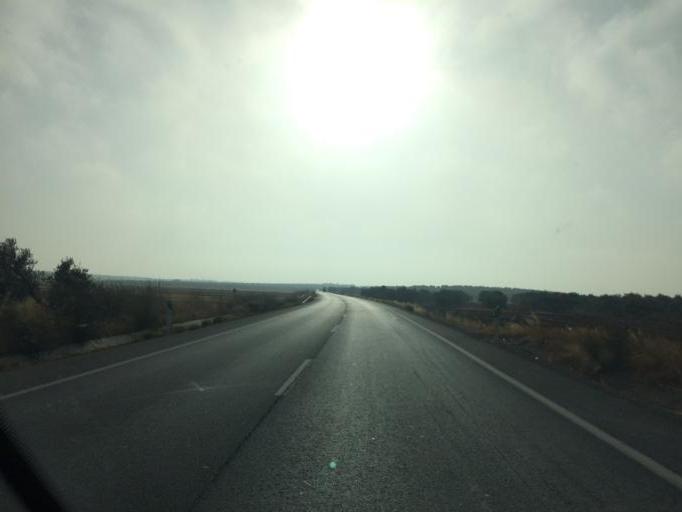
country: ES
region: Andalusia
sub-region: Provincia de Malaga
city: Campillos
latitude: 37.0478
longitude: -4.8330
